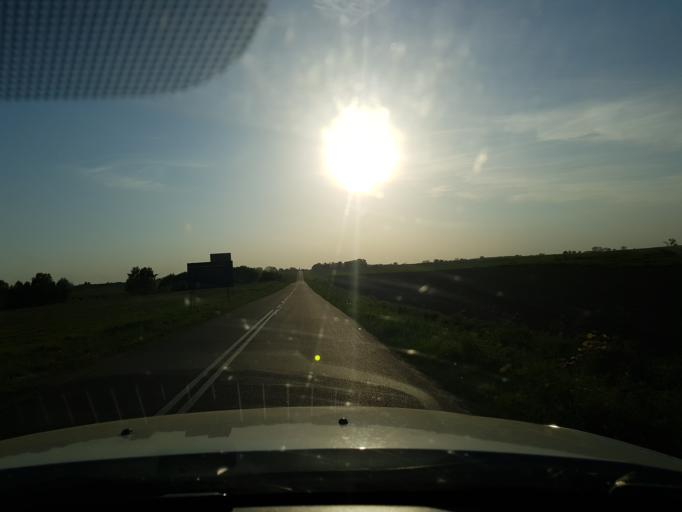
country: PL
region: West Pomeranian Voivodeship
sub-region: Powiat goleniowski
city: Maszewo
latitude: 53.4777
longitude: 15.0584
